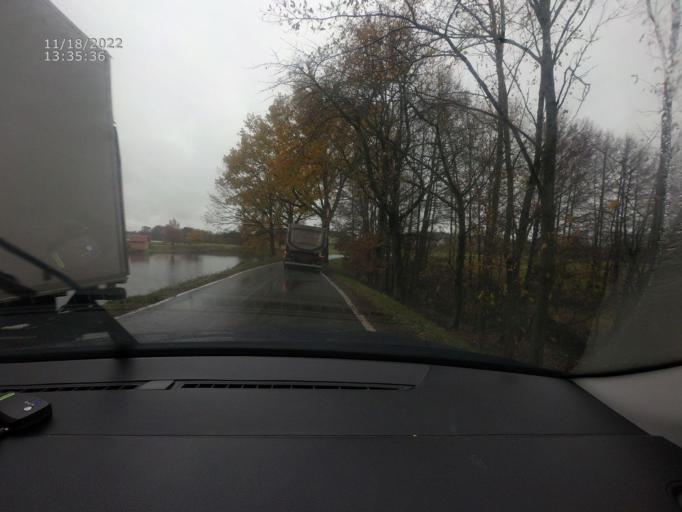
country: CZ
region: Plzensky
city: Kasejovice
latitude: 49.4098
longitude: 13.7778
